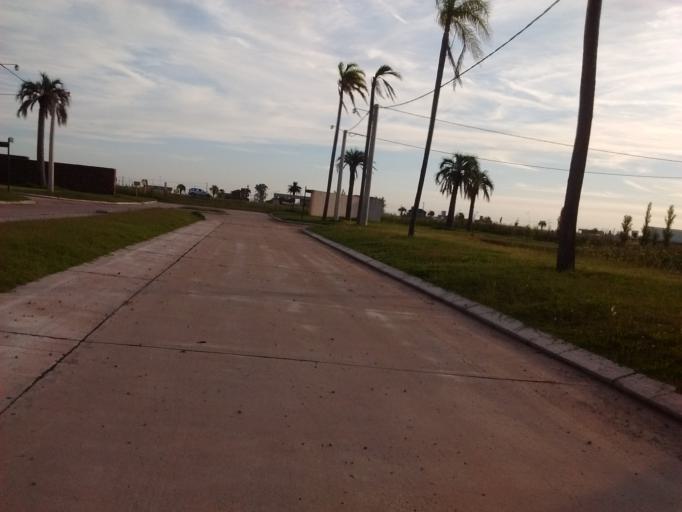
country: AR
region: Santa Fe
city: Roldan
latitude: -32.9289
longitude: -60.8747
